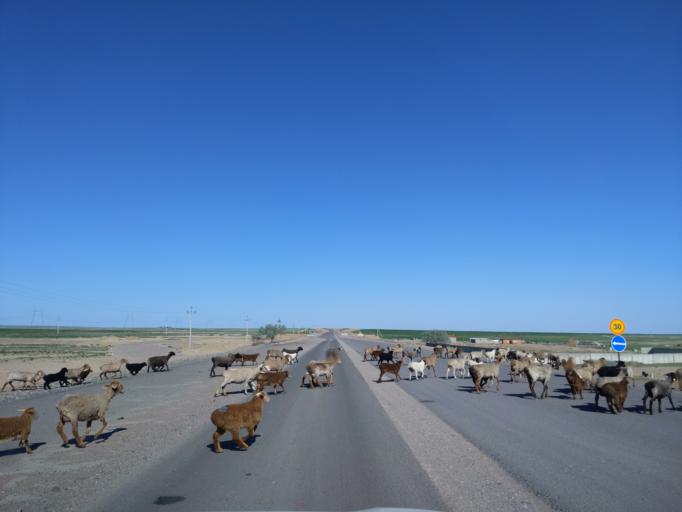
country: KZ
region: Almaty Oblysy
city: Bakanas
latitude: 44.0948
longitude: 75.9857
